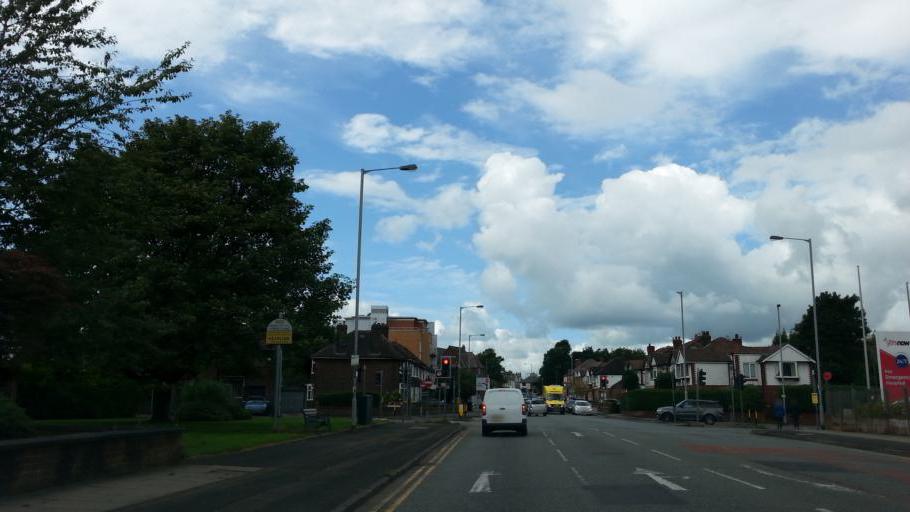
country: GB
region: England
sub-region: Borough of Bury
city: Prestwich
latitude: 53.5417
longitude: -2.2871
